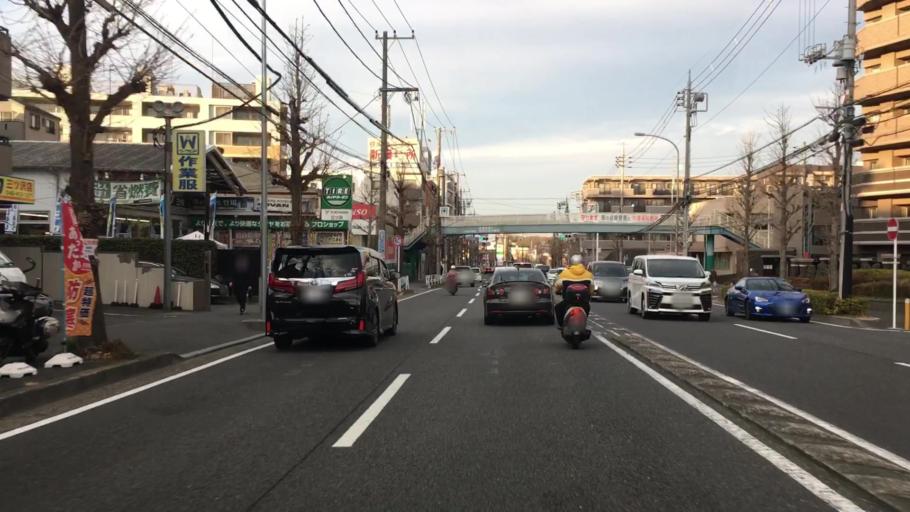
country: JP
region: Kanagawa
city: Yokohama
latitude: 35.4816
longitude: 139.6015
